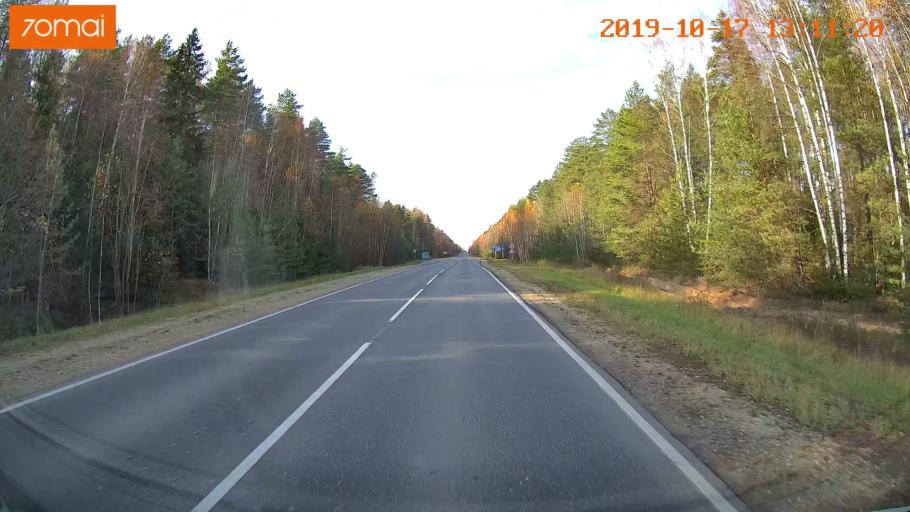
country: RU
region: Rjazan
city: Syntul
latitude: 55.0267
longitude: 41.2378
